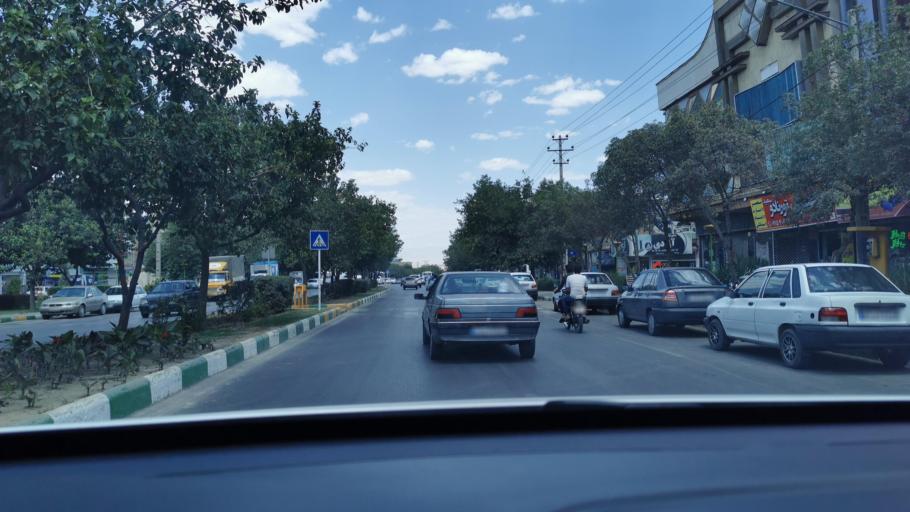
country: IR
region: Razavi Khorasan
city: Mashhad
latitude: 36.3448
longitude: 59.6262
